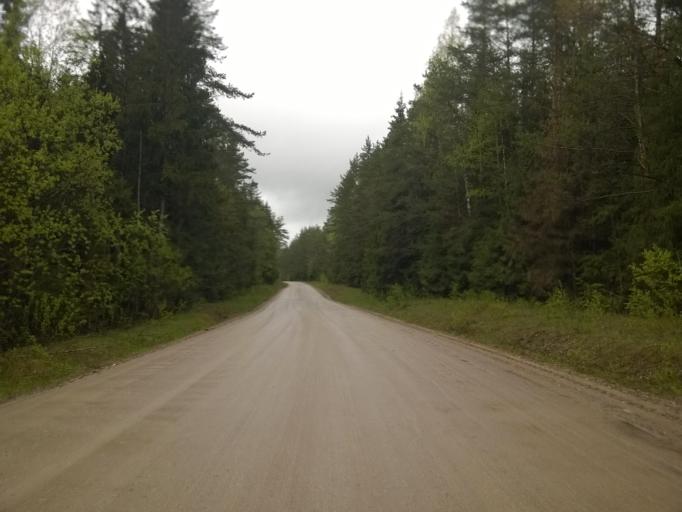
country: LV
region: Amatas Novads
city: Drabesi
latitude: 57.2115
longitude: 25.2348
